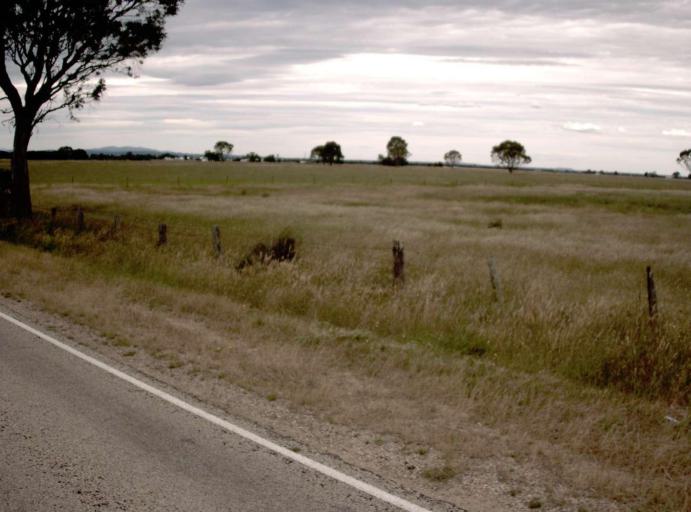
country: AU
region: Victoria
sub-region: East Gippsland
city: Bairnsdale
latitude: -37.8917
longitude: 147.5564
